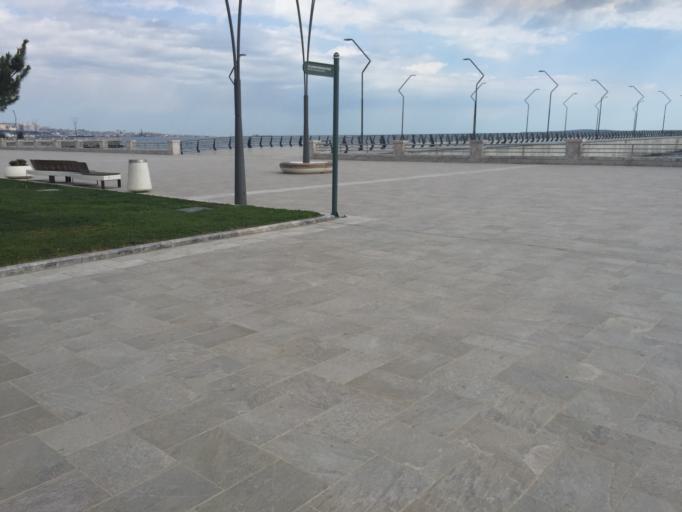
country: AZ
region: Baki
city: Baku
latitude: 40.3744
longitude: 49.8818
